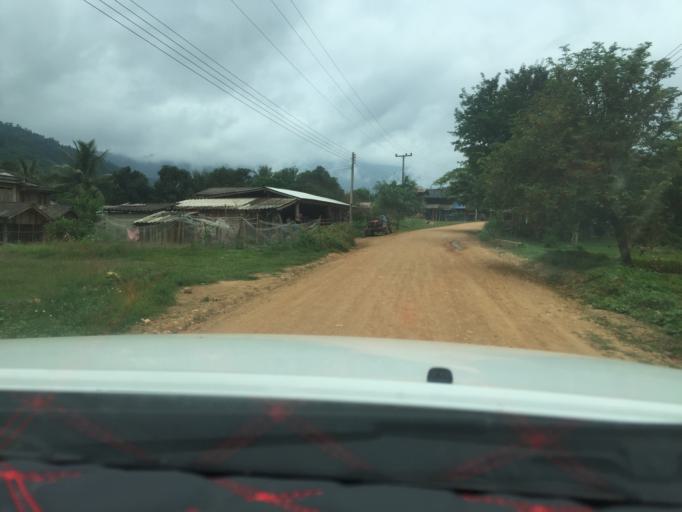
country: TH
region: Phayao
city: Phu Sang
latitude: 19.7379
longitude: 100.4686
